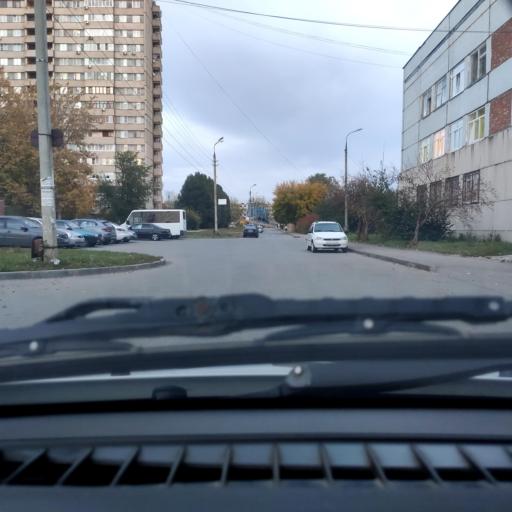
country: RU
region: Samara
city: Tol'yatti
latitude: 53.5296
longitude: 49.3924
